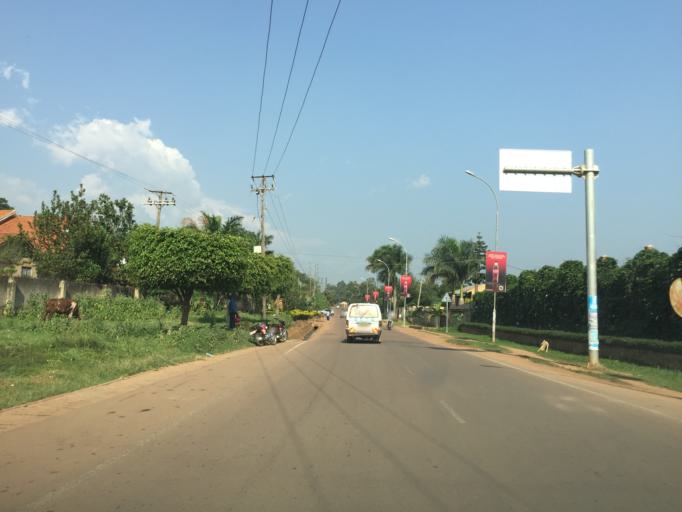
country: UG
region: Central Region
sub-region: Kampala District
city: Kampala
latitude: 0.2393
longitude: 32.6215
